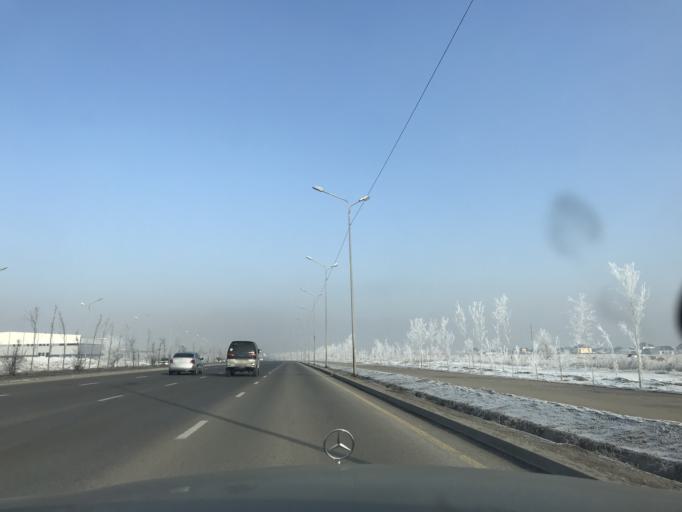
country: KZ
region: Almaty Oblysy
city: Burunday
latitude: 43.3271
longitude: 76.8340
